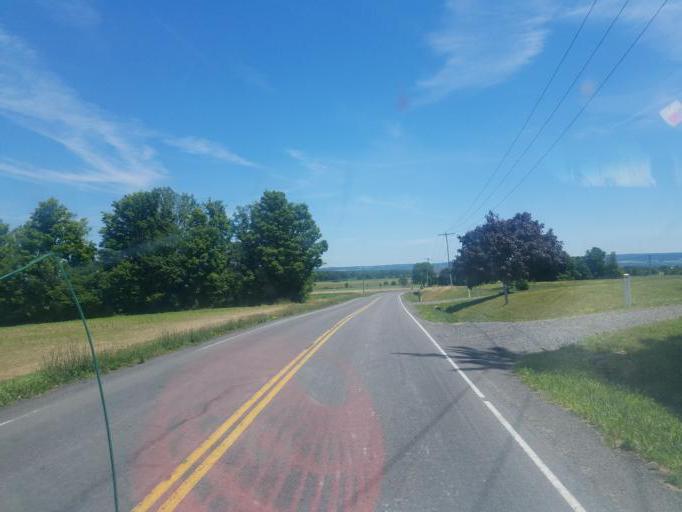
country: US
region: New York
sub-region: Yates County
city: Penn Yan
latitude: 42.6231
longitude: -76.9860
